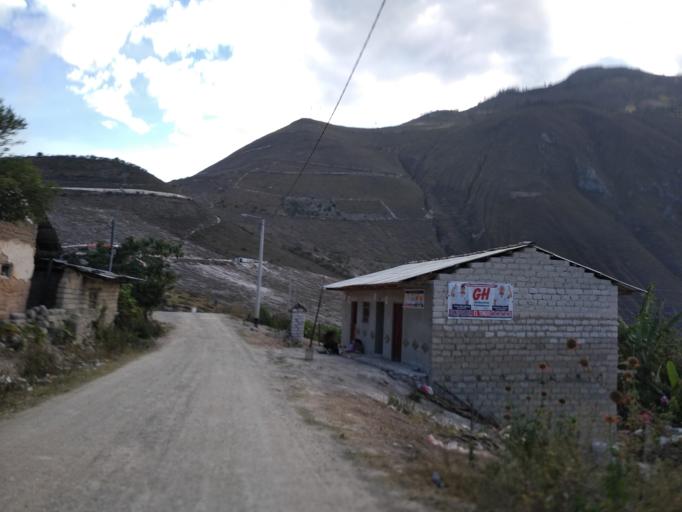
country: PE
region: Amazonas
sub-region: Provincia de Luya
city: Tingo
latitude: -6.3719
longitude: -77.9118
